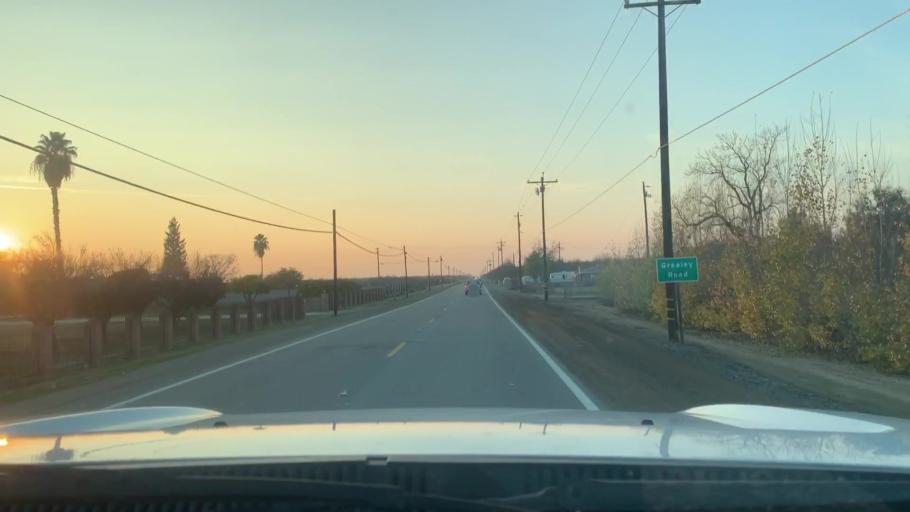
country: US
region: California
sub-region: Kern County
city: Rosedale
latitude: 35.3835
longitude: -119.2144
